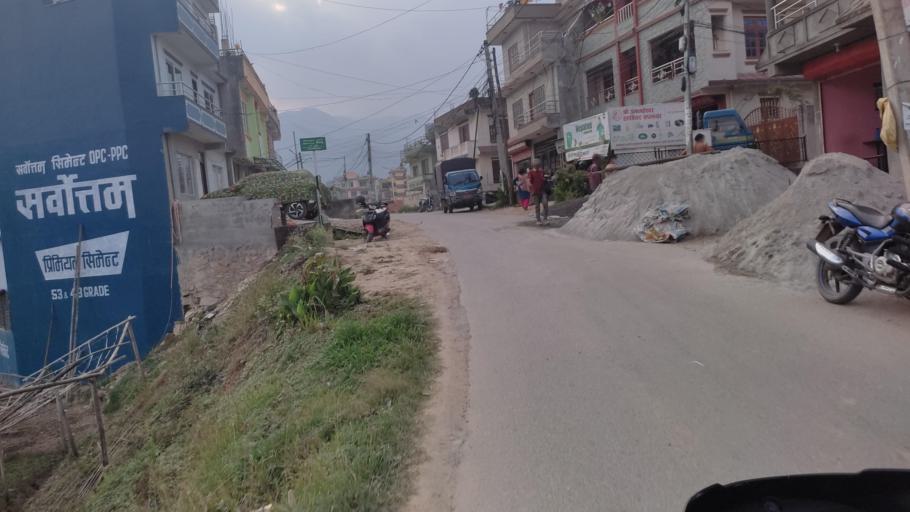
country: NP
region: Central Region
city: Kirtipur
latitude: 27.6786
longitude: 85.2569
